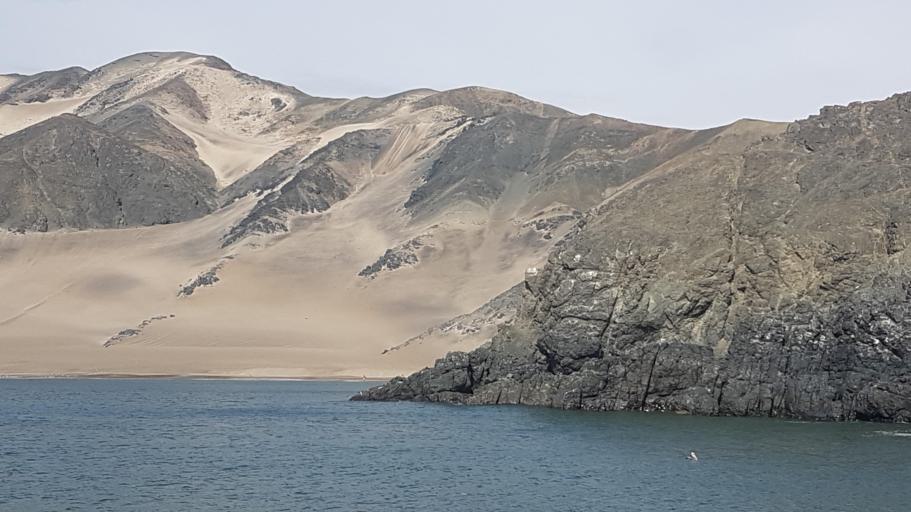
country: PE
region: Ancash
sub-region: Provincia de Santa
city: Samanco
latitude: -9.2530
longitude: -78.4948
